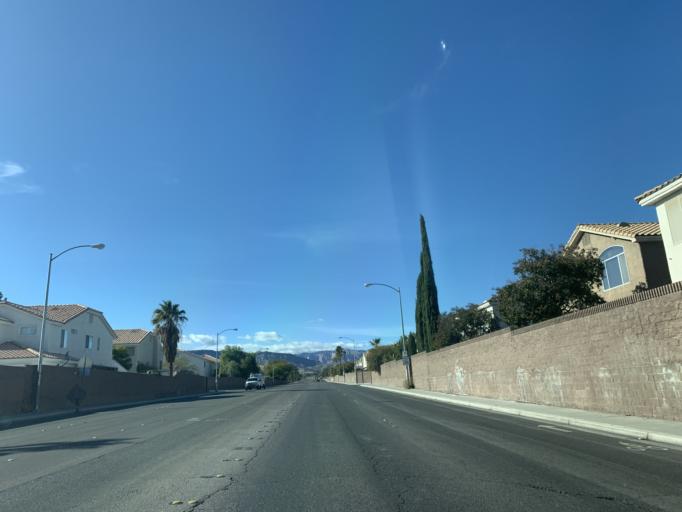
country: US
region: Nevada
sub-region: Clark County
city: Summerlin South
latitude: 36.1225
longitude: -115.3064
